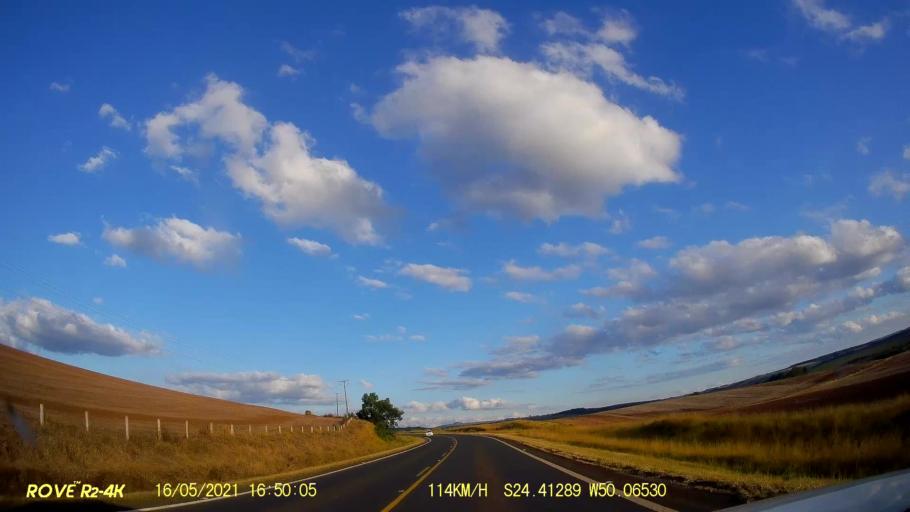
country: BR
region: Parana
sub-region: Pirai Do Sul
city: Pirai do Sul
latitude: -24.4132
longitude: -50.0651
